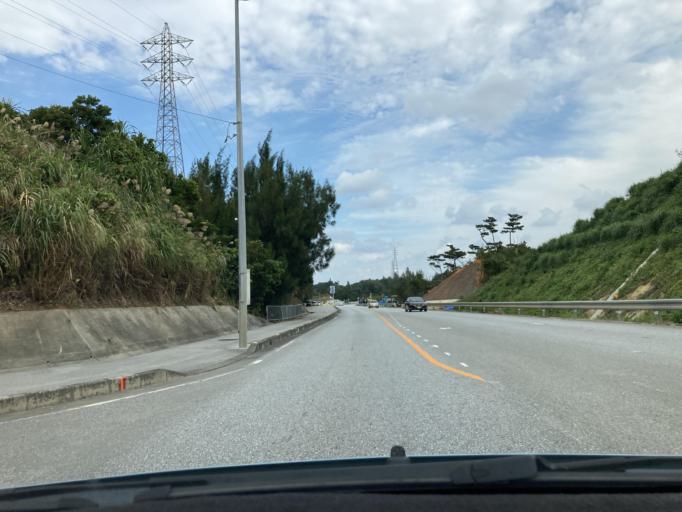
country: JP
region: Okinawa
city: Ishikawa
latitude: 26.4973
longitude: 127.8608
